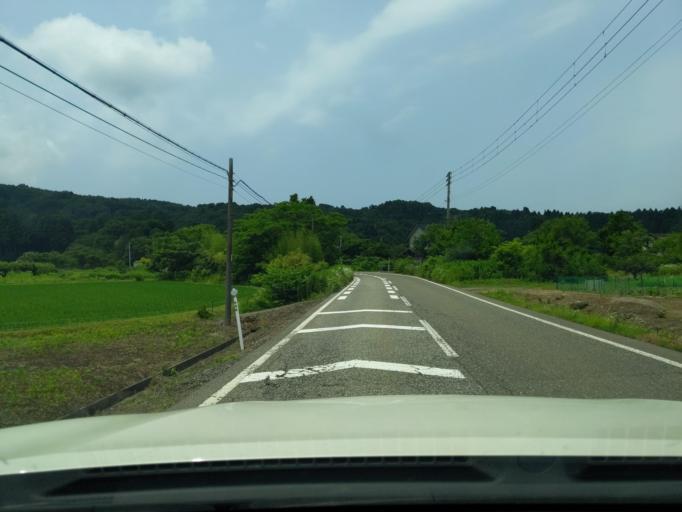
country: JP
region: Niigata
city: Kashiwazaki
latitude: 37.3326
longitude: 138.5585
